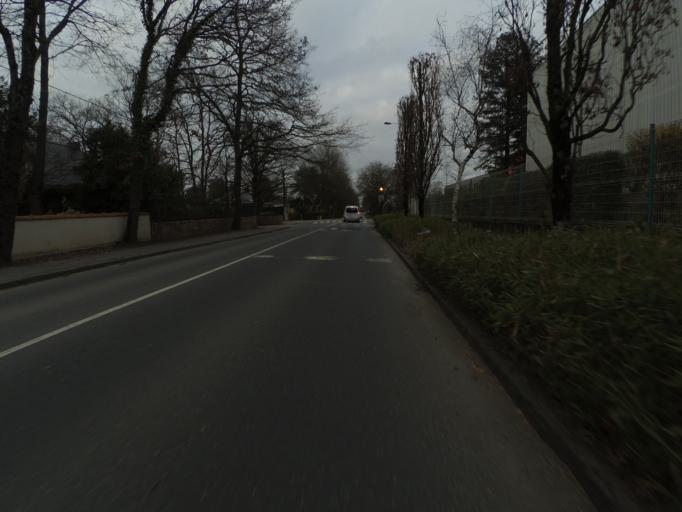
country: FR
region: Pays de la Loire
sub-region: Departement de la Loire-Atlantique
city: Carquefou
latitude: 47.2778
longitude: -1.4943
